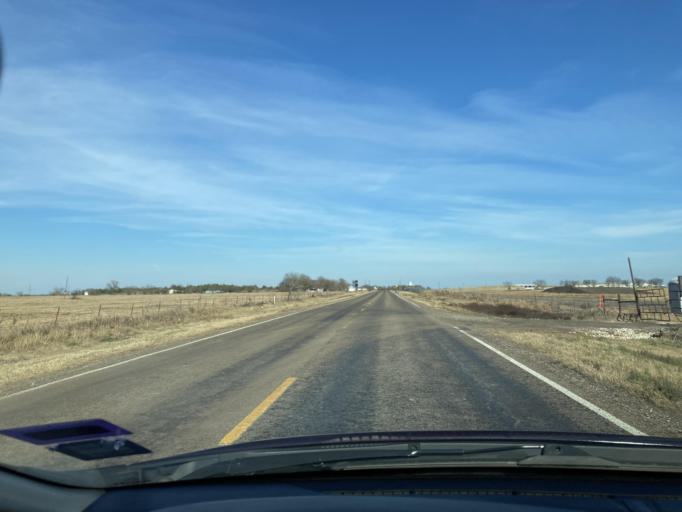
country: US
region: Texas
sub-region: Navarro County
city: Corsicana
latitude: 32.0322
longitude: -96.4063
